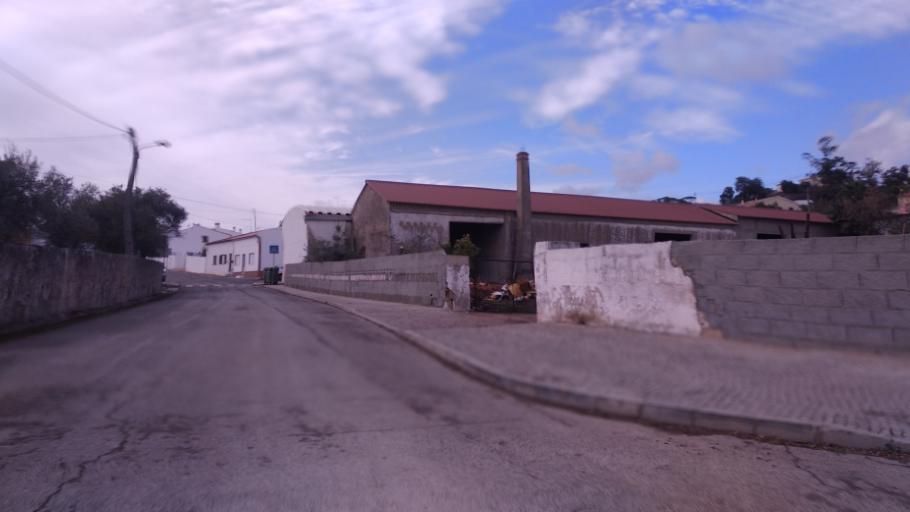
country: PT
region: Faro
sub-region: Sao Bras de Alportel
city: Sao Bras de Alportel
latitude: 37.1757
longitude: -7.9065
